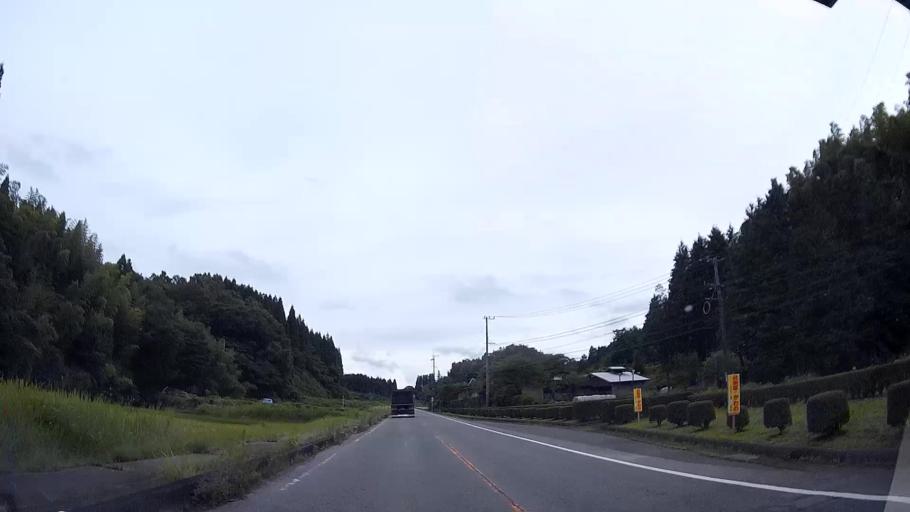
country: JP
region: Oita
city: Tsukawaki
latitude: 33.1256
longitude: 131.0384
